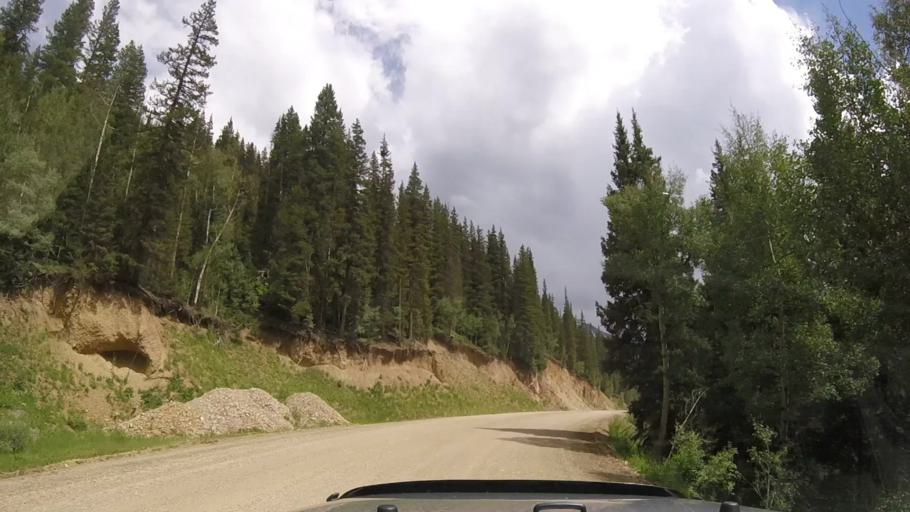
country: US
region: Colorado
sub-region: San Juan County
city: Silverton
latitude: 37.8337
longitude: -107.6723
